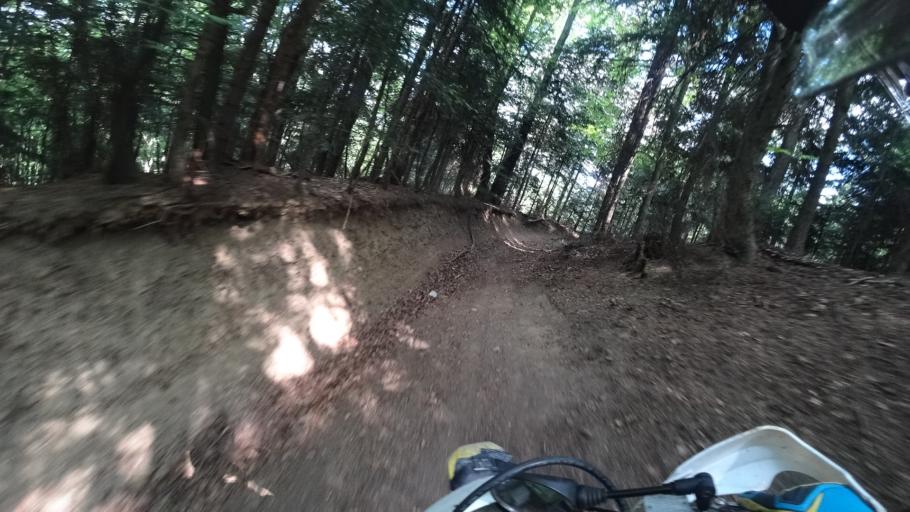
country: HR
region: Grad Zagreb
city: Kasina
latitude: 45.9241
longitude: 15.9495
